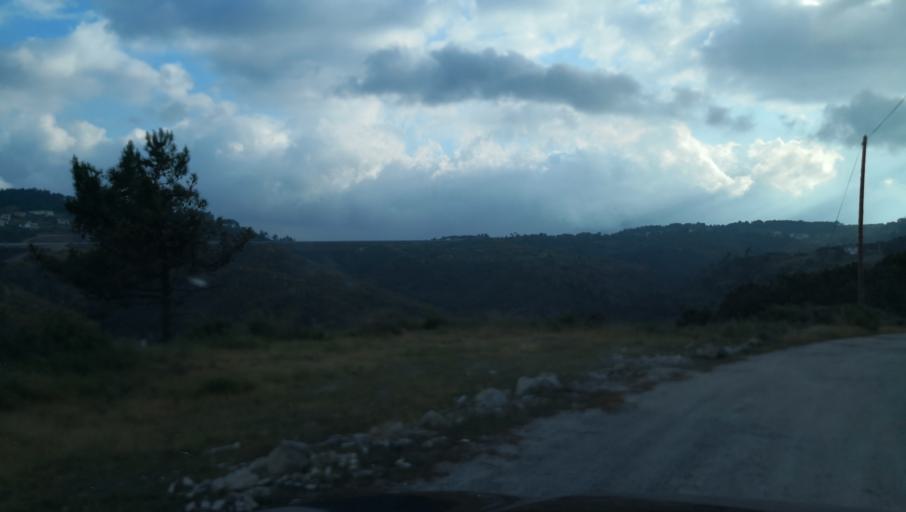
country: PT
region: Vila Real
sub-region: Vila Real
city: Vila Real
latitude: 41.2730
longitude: -7.7856
